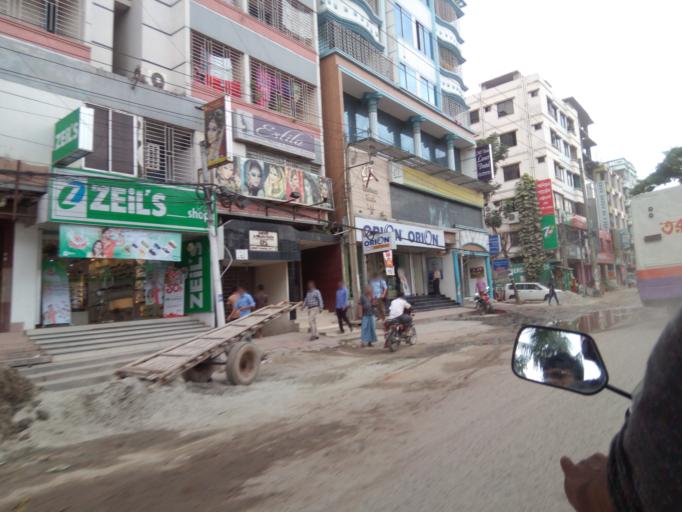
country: BD
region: Dhaka
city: Paltan
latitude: 23.7641
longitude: 90.4307
